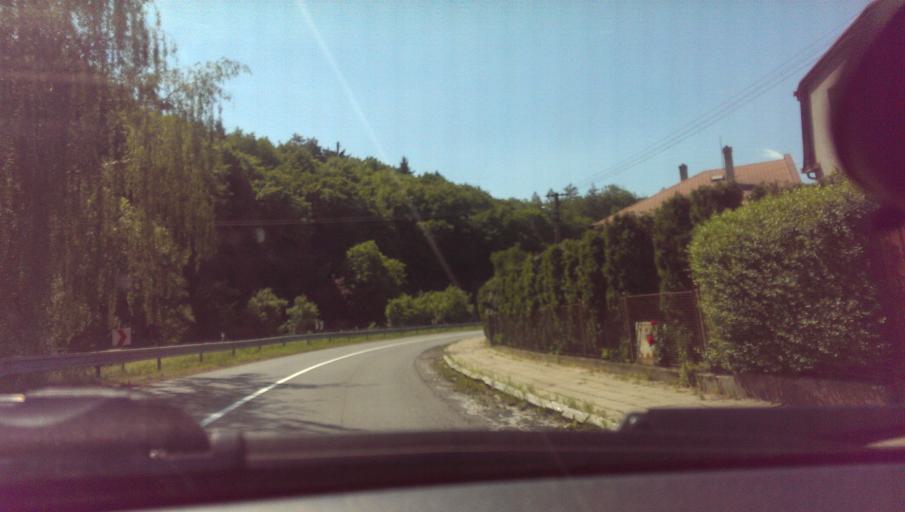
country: CZ
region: Zlin
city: Breznice
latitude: 49.1594
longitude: 17.6340
